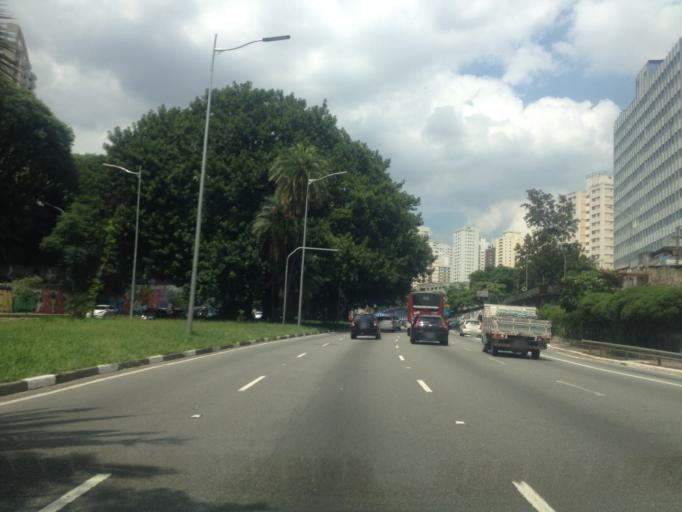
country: BR
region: Sao Paulo
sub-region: Sao Paulo
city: Sao Paulo
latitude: -23.5591
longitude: -46.6390
